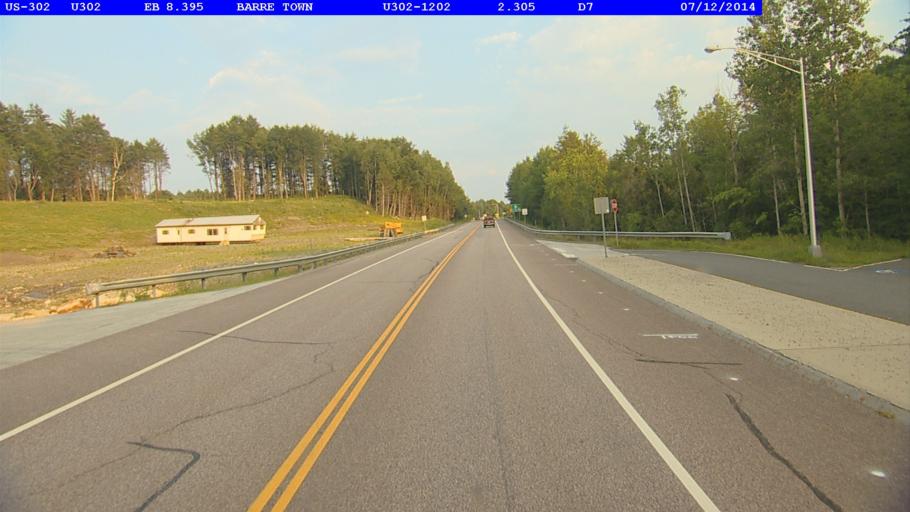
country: US
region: Vermont
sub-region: Washington County
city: South Barre
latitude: 44.1638
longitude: -72.4513
